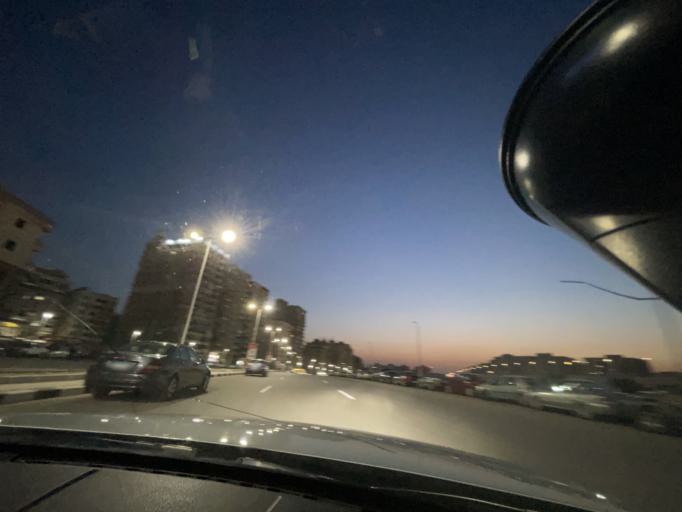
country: EG
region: Muhafazat al Qahirah
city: Cairo
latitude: 30.0699
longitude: 31.3551
